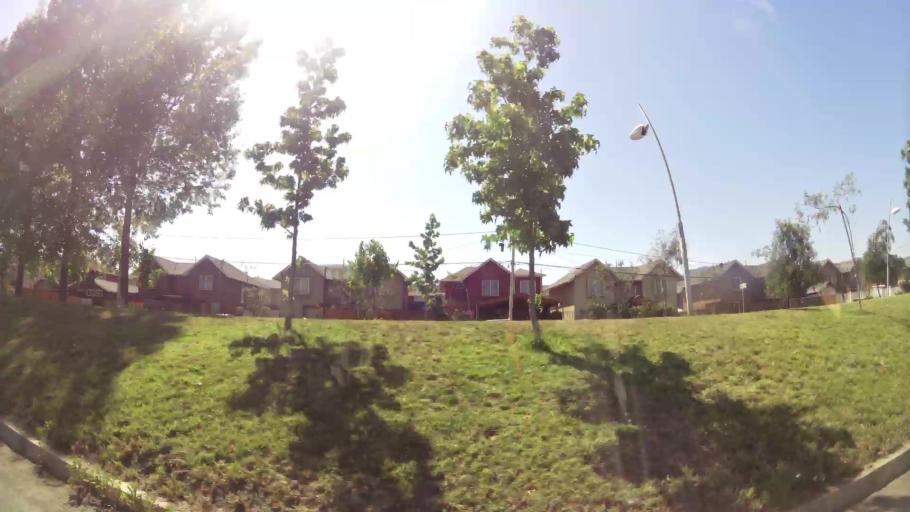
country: CL
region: Santiago Metropolitan
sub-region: Provincia de Maipo
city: San Bernardo
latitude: -33.6120
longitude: -70.6879
